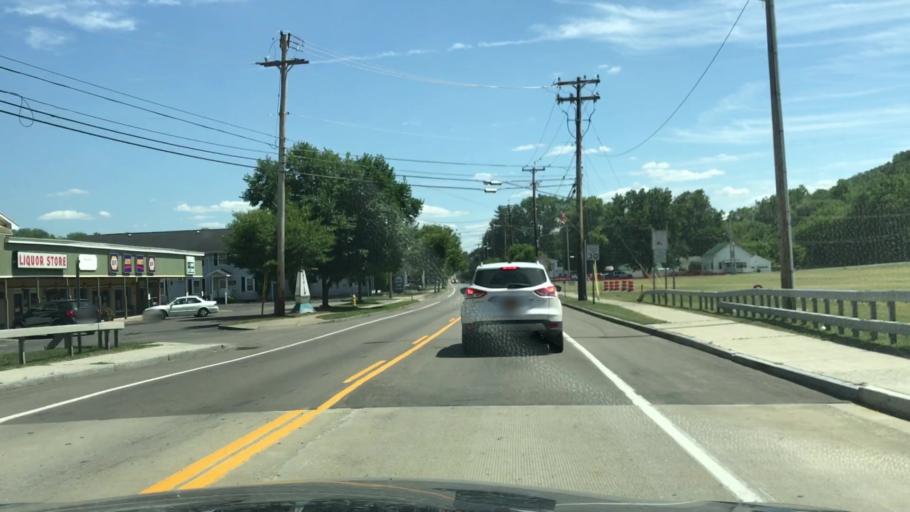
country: US
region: New York
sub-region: Livingston County
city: Mount Morris
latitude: 42.7379
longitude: -77.8813
